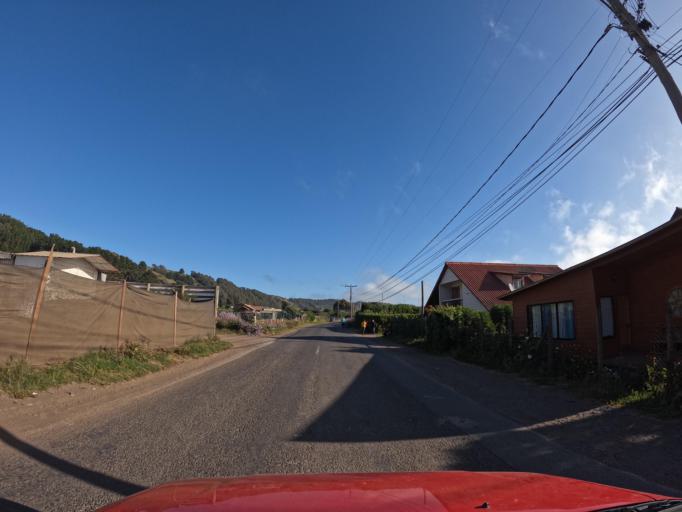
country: CL
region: Maule
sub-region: Provincia de Talca
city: Constitucion
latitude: -34.9256
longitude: -72.1794
